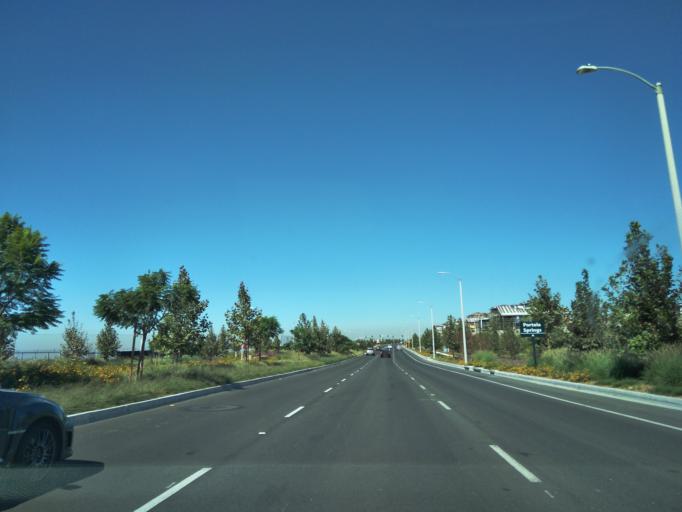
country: US
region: California
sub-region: Orange County
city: Lake Forest
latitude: 33.6735
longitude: -117.7100
